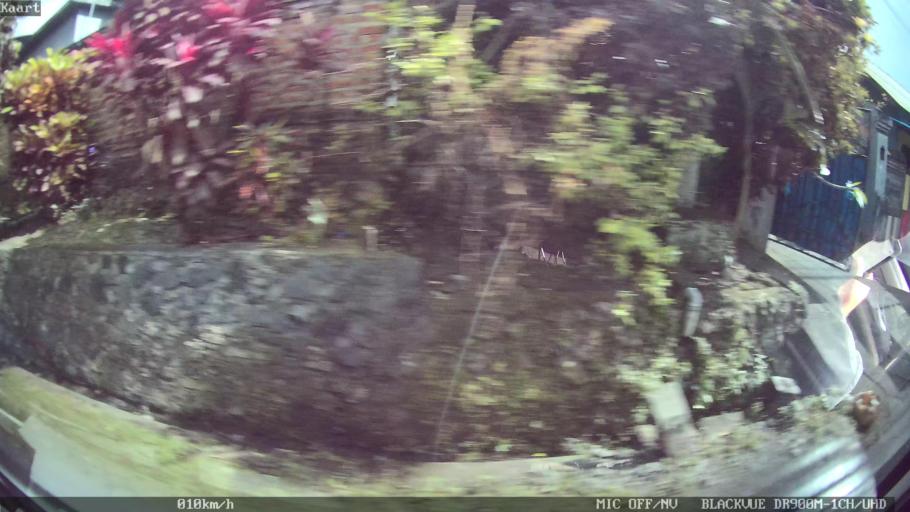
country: ID
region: Bali
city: Banjar Karangsuling
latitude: -8.6114
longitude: 115.2006
